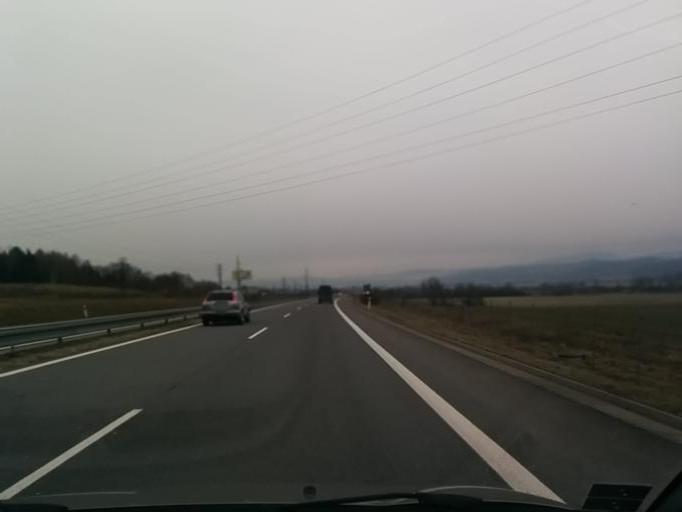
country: SK
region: Banskobystricky
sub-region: Okres Banska Bystrica
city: Zvolen
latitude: 48.5926
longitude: 19.0980
